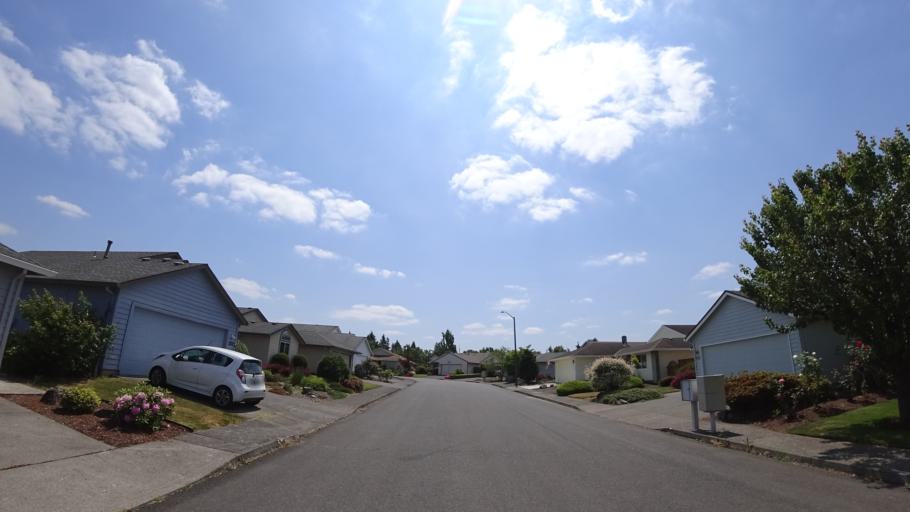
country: US
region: Oregon
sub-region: Multnomah County
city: Fairview
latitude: 45.5396
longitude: -122.5039
